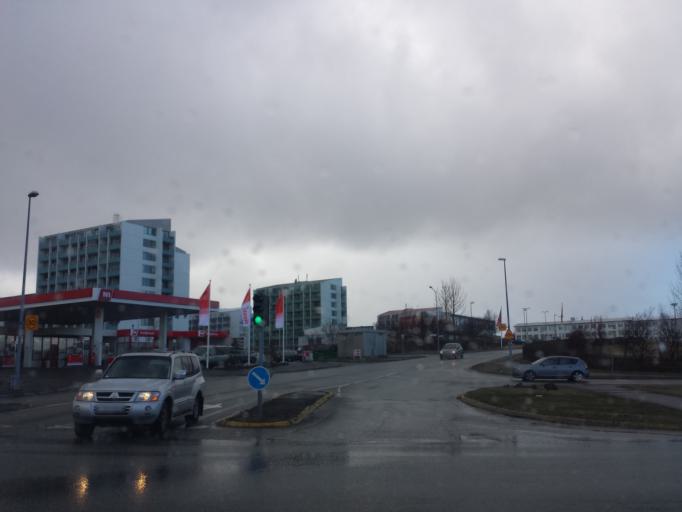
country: IS
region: Capital Region
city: Reykjavik
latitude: 64.1103
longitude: -21.8554
